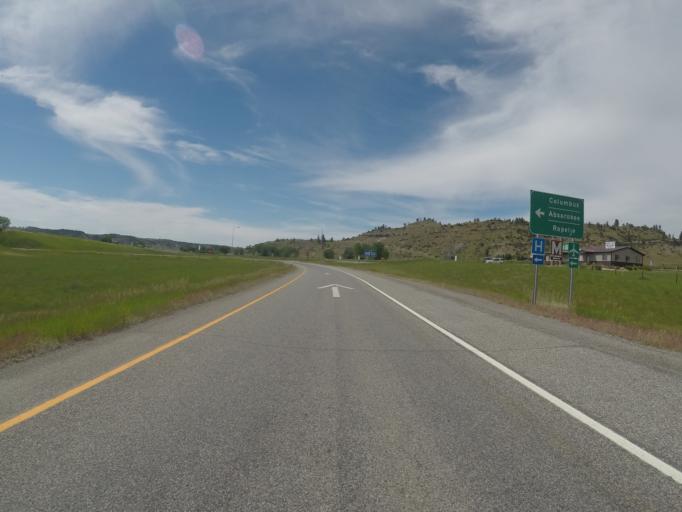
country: US
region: Montana
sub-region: Stillwater County
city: Columbus
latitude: 45.6470
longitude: -109.2461
